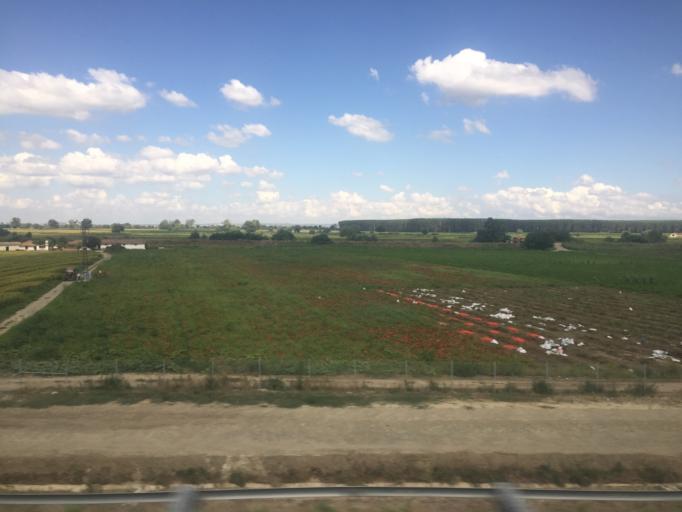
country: TR
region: Bursa
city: Tatkavakli
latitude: 40.0846
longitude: 28.2636
